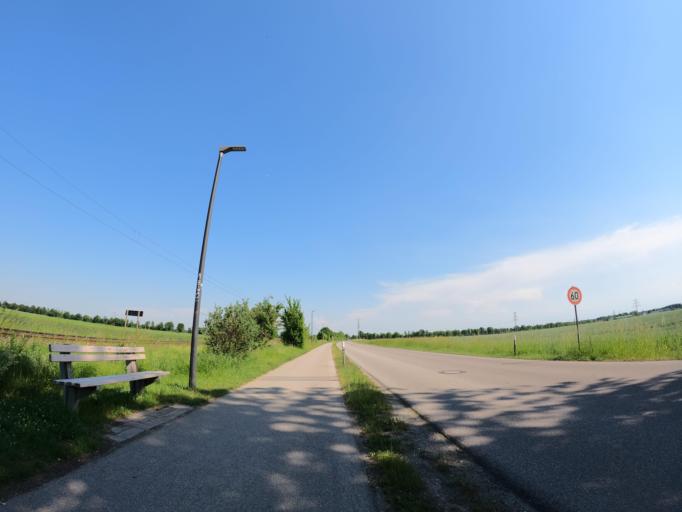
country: DE
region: Bavaria
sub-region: Upper Bavaria
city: Hohenbrunn
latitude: 48.0565
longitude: 11.6881
